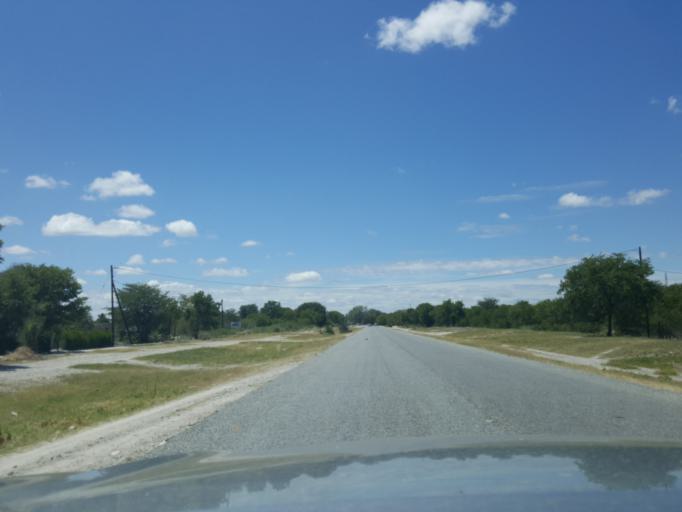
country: BW
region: Central
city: Nata
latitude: -20.2127
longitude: 26.1739
